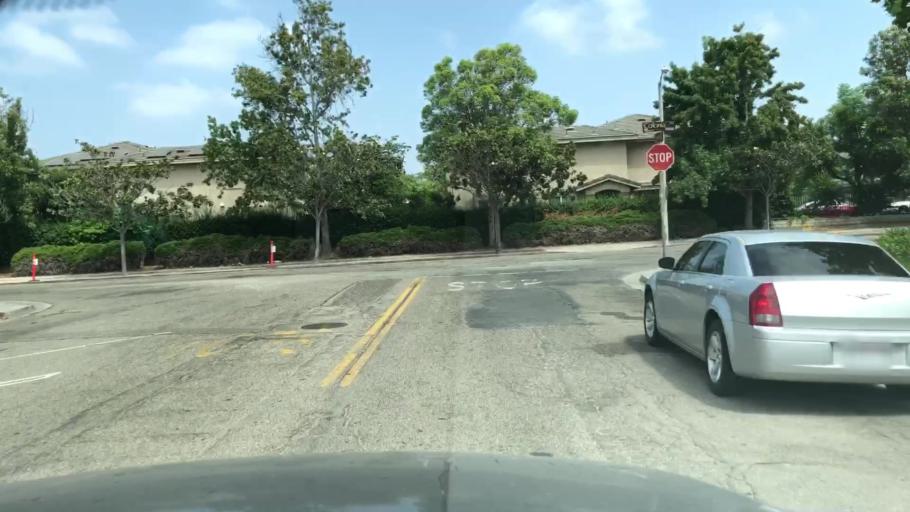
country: US
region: California
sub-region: Ventura County
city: Oxnard
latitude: 34.2061
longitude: -119.1663
